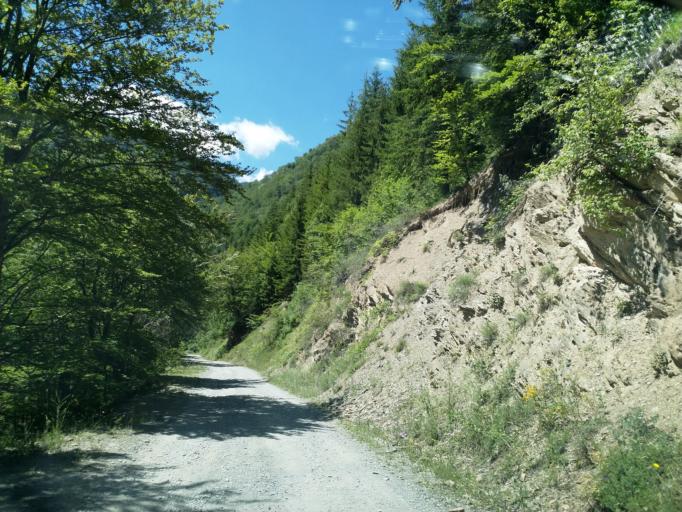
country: XK
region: Mitrovica
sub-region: Komuna e Leposaviqit
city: Leposaviq
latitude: 43.2784
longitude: 20.8702
